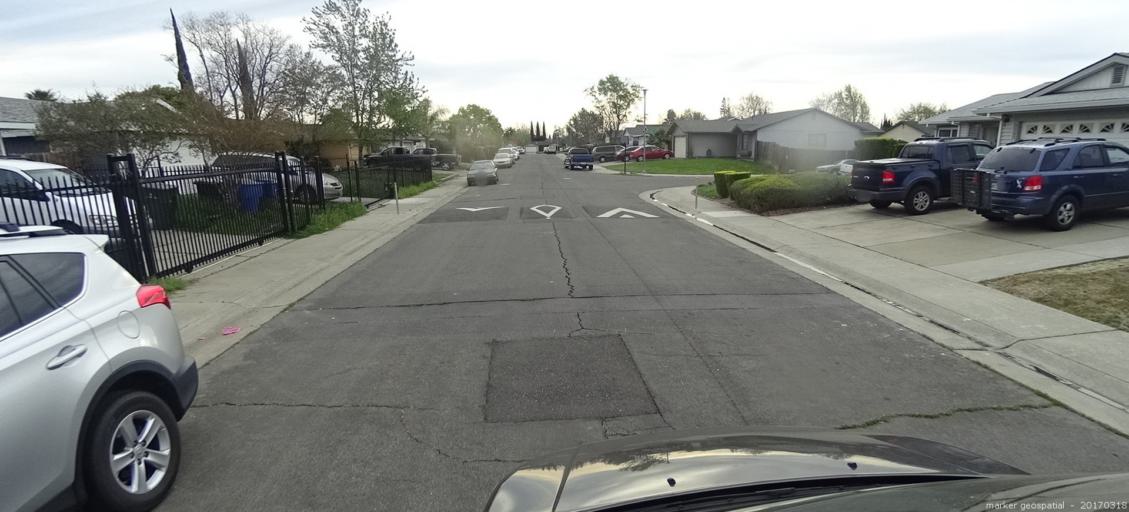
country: US
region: California
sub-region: Sacramento County
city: Parkway
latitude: 38.4884
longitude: -121.4671
